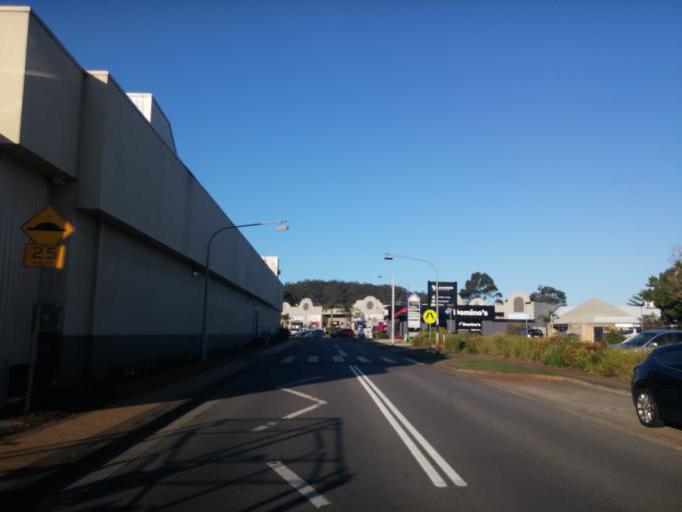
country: AU
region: New South Wales
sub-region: Port Stephens Shire
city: Corlette
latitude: -32.7370
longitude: 152.1074
